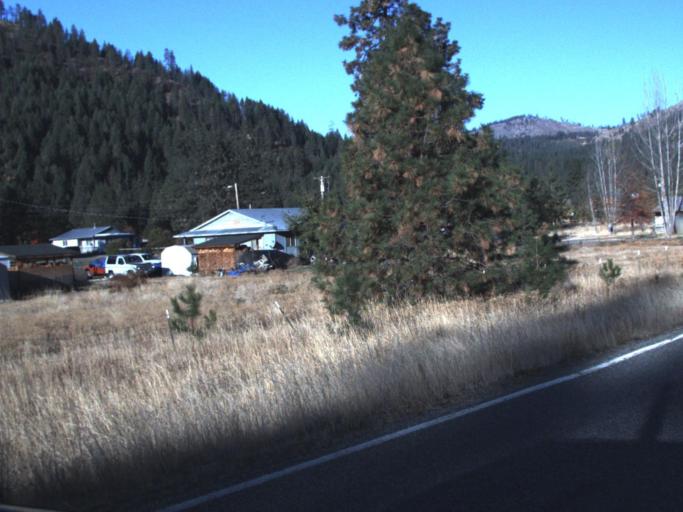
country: US
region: Washington
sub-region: Okanogan County
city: Coulee Dam
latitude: 48.0761
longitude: -118.6812
